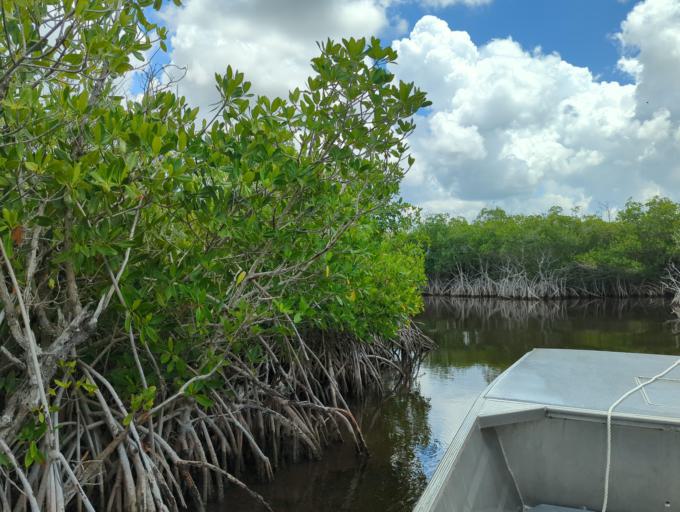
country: US
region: Florida
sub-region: Collier County
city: Marco
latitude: 25.9031
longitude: -81.3738
